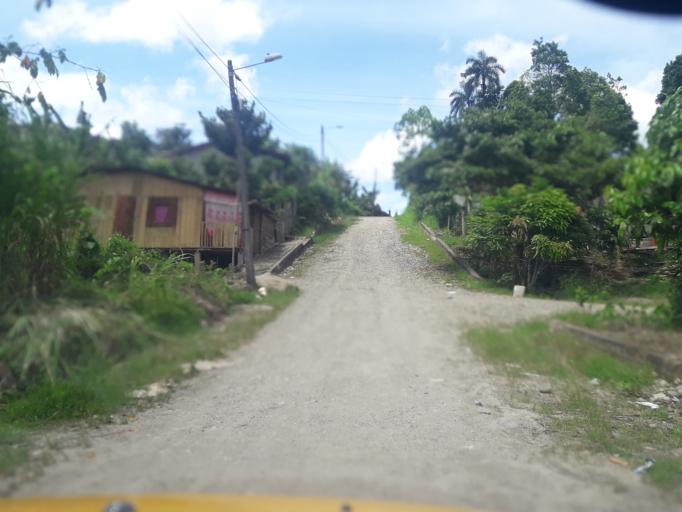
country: EC
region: Napo
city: Tena
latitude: -1.0051
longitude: -77.8216
